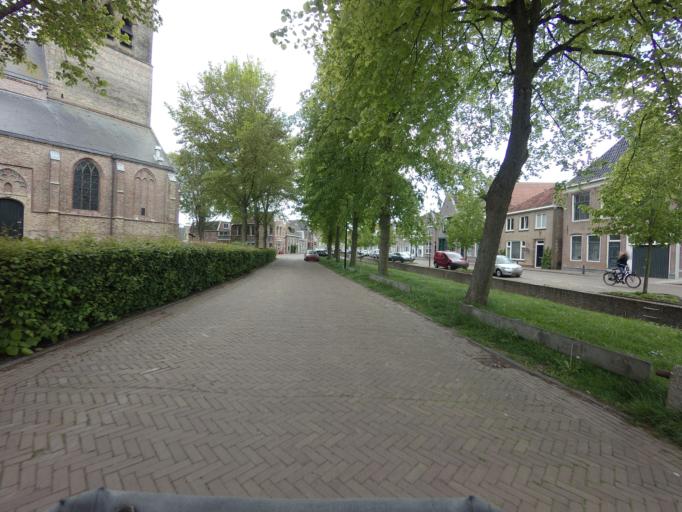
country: NL
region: Friesland
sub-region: Sudwest Fryslan
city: Bolsward
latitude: 53.0652
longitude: 5.5261
